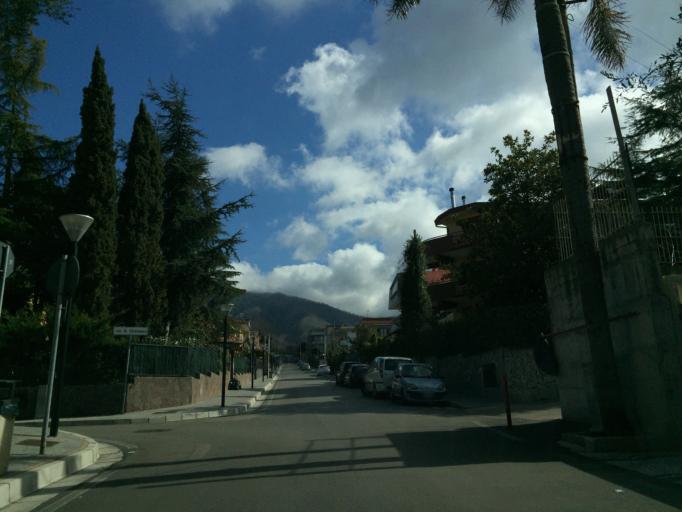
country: IT
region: Campania
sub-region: Provincia di Napoli
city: Pollena Trocchia
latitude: 40.8513
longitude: 14.3757
